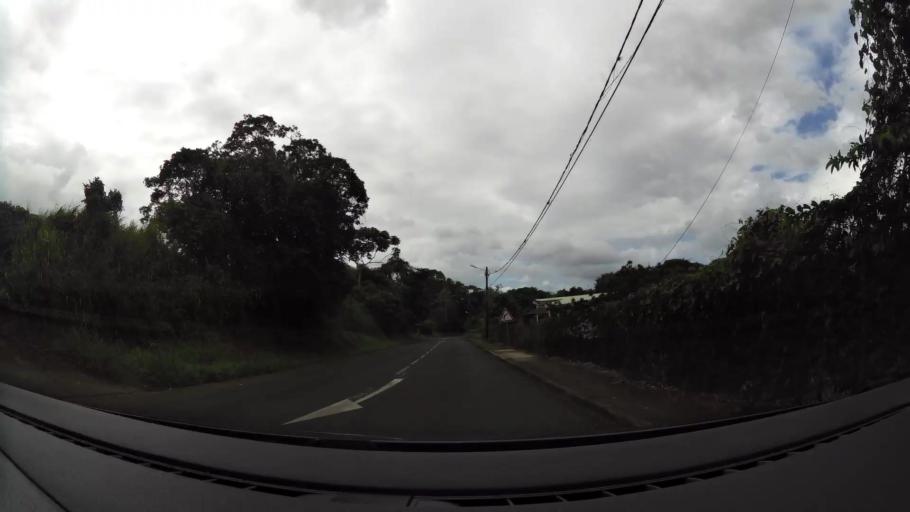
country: GP
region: Guadeloupe
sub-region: Guadeloupe
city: Lamentin
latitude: 16.2639
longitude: -61.6264
